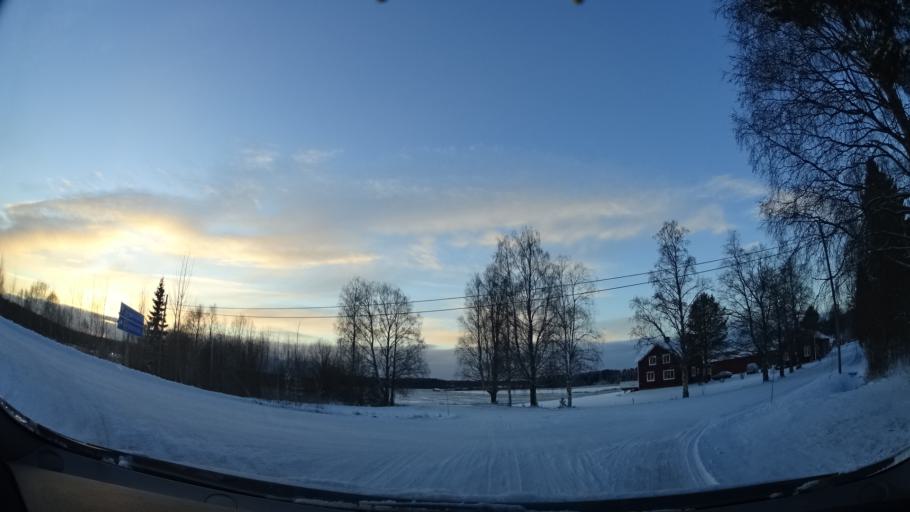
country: SE
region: Vaesterbotten
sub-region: Skelleftea Kommun
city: Kage
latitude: 64.8518
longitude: 20.9932
